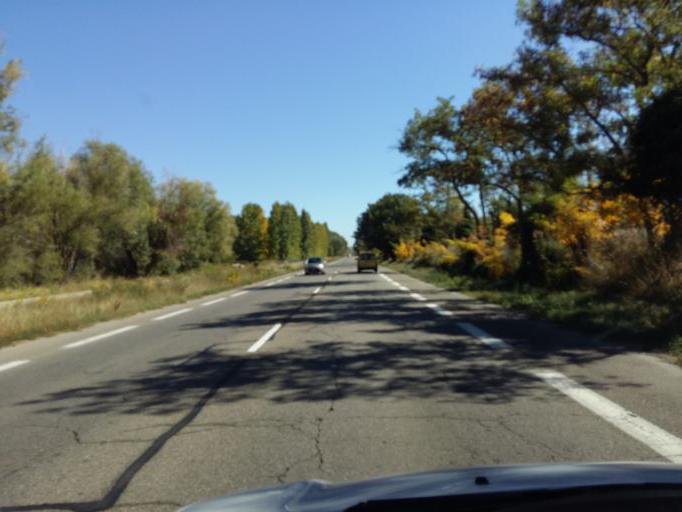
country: FR
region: Provence-Alpes-Cote d'Azur
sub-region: Departement du Vaucluse
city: Lauris
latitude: 43.7500
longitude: 5.2747
